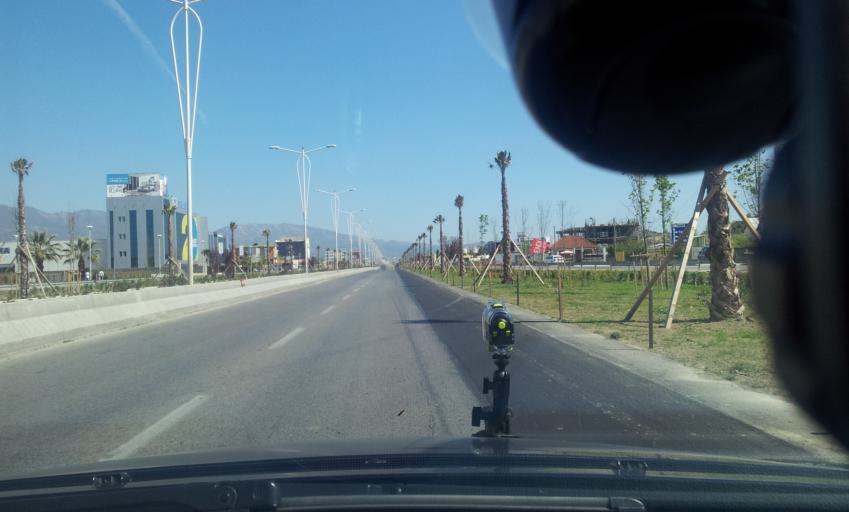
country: AL
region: Tirane
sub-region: Rrethi i Tiranes
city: Kashar
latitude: 41.3600
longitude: 19.7269
